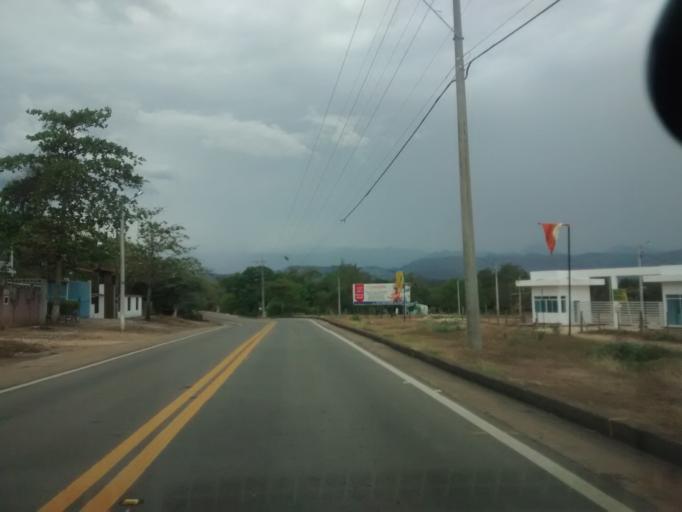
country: CO
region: Cundinamarca
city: Tocaima
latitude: 4.4342
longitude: -74.6845
